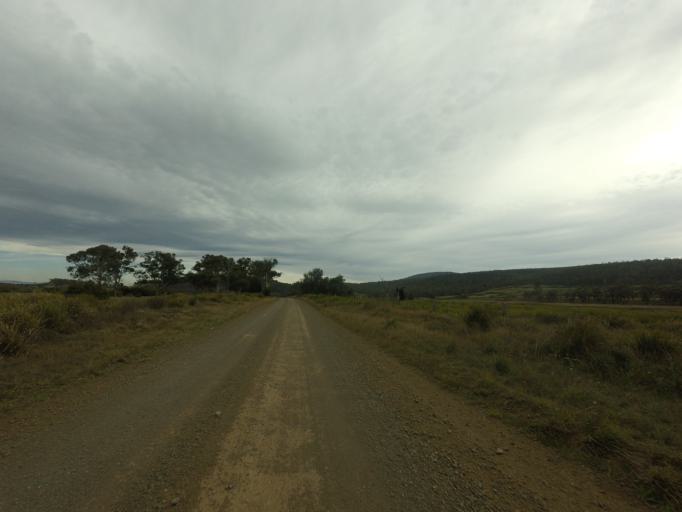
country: AU
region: Tasmania
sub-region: Derwent Valley
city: New Norfolk
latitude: -42.3980
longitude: 146.9562
